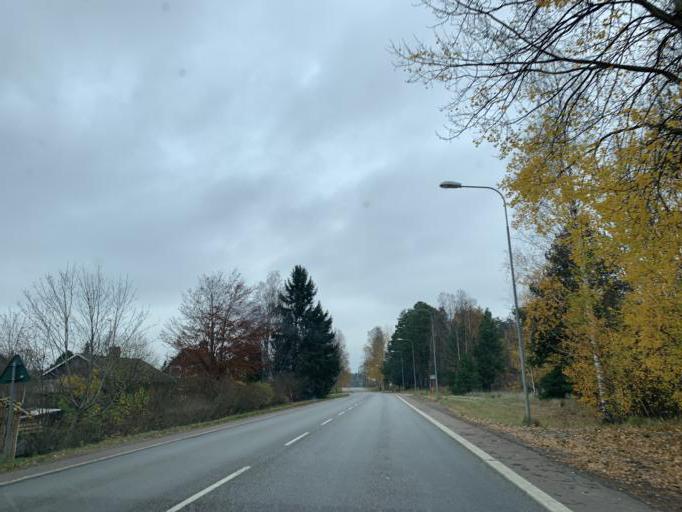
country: SE
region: Vaestmanland
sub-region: Surahammars Kommun
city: Ramnas
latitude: 59.7717
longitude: 16.1998
